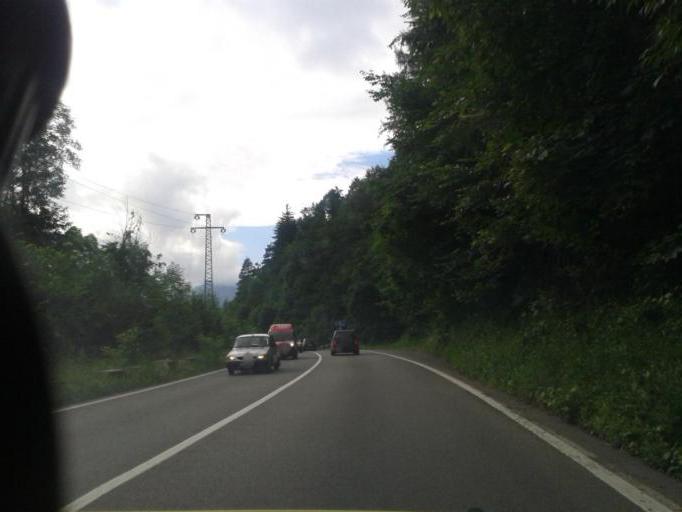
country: RO
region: Prahova
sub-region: Comuna Comarnic
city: Posada
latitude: 45.3033
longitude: 25.5848
